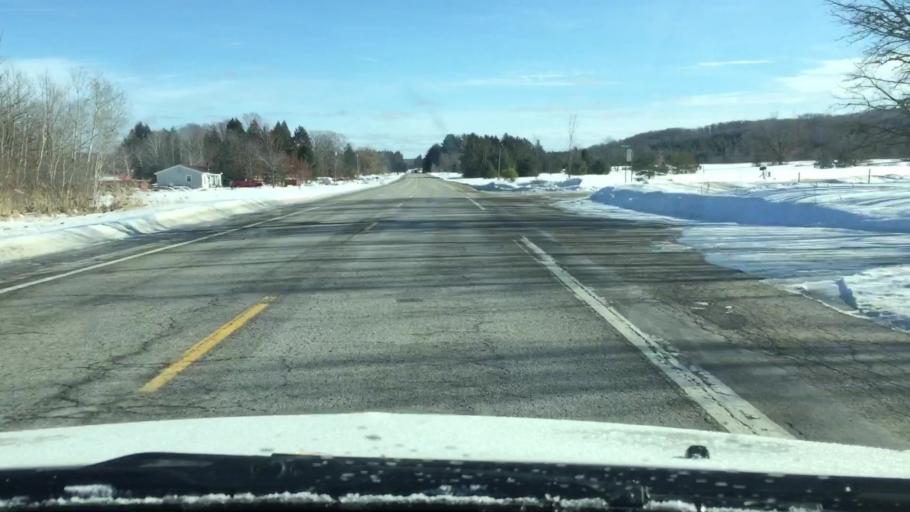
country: US
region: Michigan
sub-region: Charlevoix County
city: East Jordan
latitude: 45.1008
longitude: -85.1144
